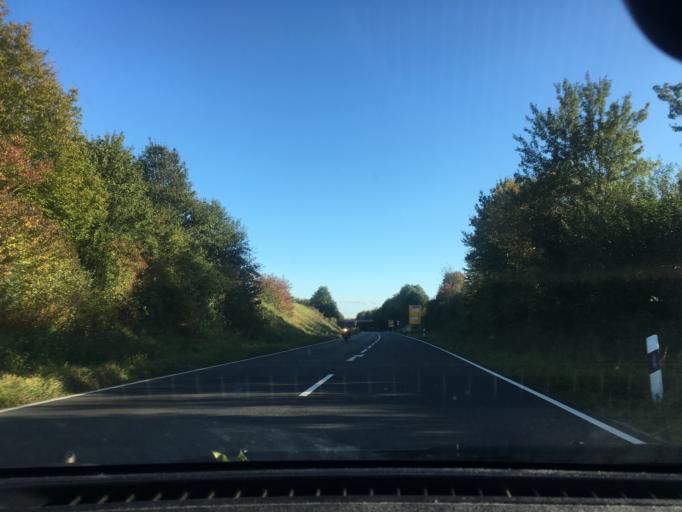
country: DE
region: Lower Saxony
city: Einbeck
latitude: 51.8237
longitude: 9.8315
